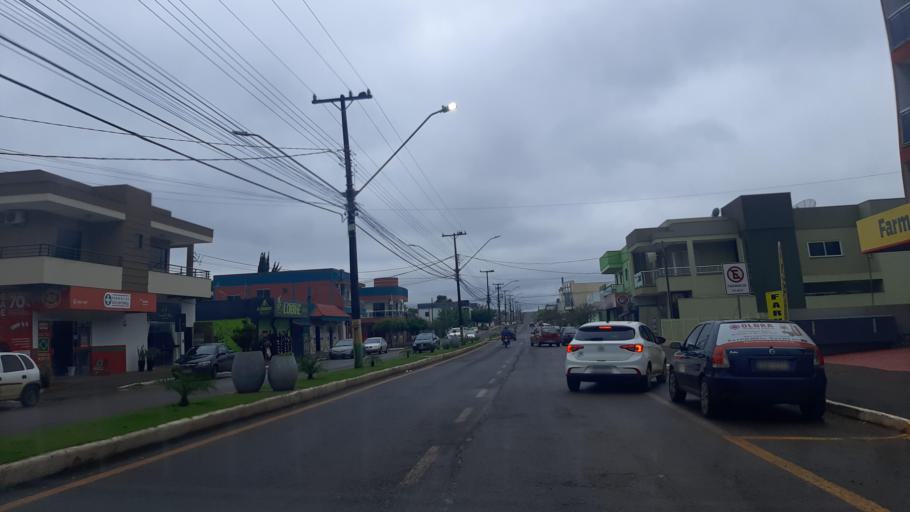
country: BR
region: Parana
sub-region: Santo Antonio Do Sudoeste
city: Santo Antonio do Sudoeste
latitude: -26.0621
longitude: -53.7261
